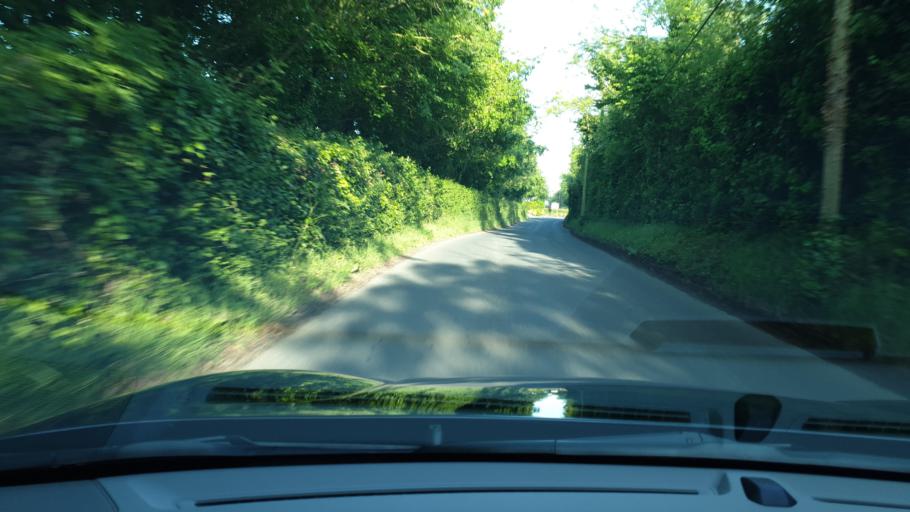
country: IE
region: Leinster
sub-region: An Mhi
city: Ashbourne
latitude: 53.5366
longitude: -6.3233
